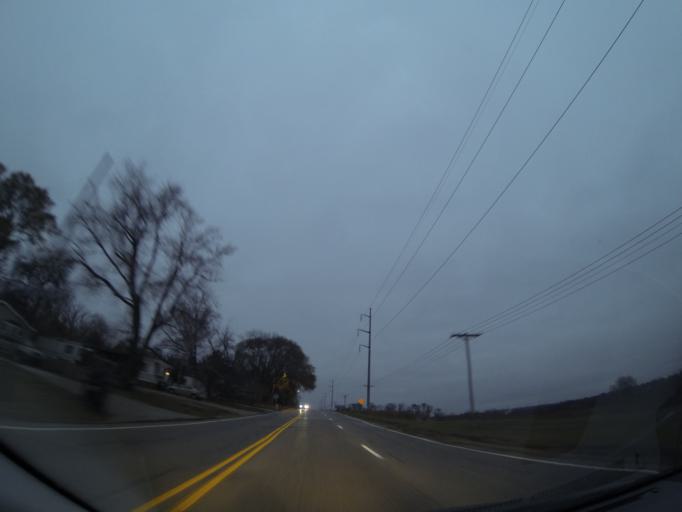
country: US
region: Nebraska
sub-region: Douglas County
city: Elkhorn
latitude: 41.2674
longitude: -96.1772
